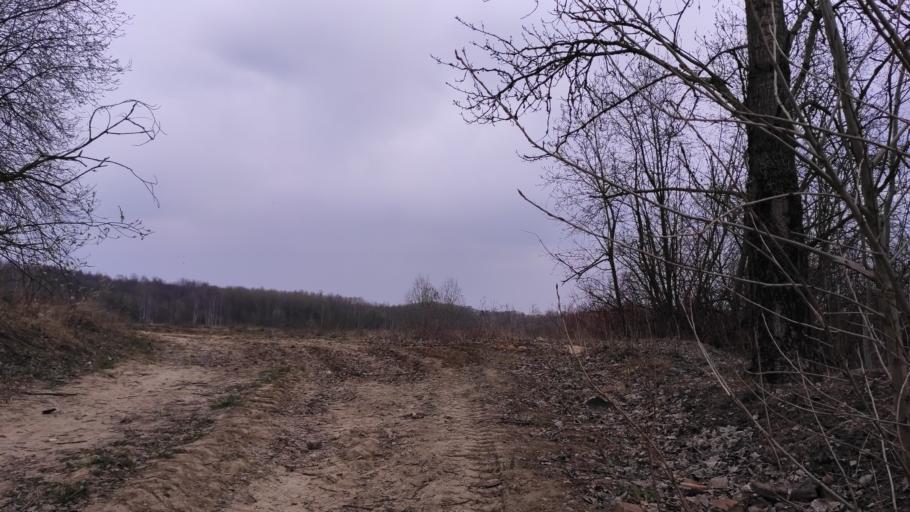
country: BY
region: Minsk
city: Novoye Medvezhino
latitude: 53.8833
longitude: 27.4664
